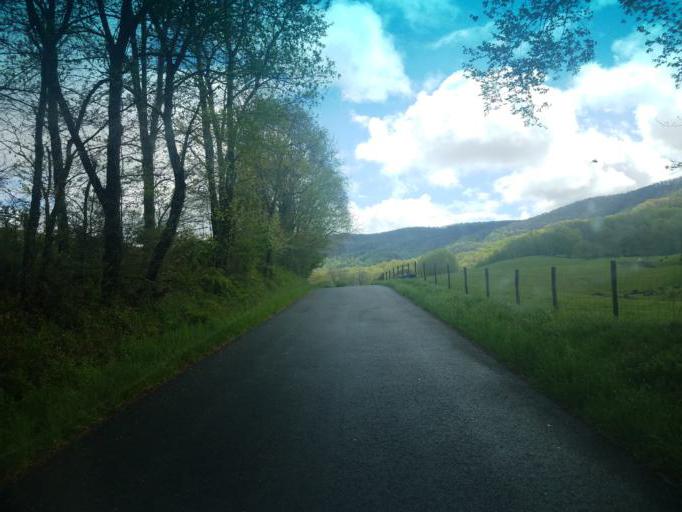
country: US
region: Virginia
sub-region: Smyth County
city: Atkins
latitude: 36.9542
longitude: -81.4054
